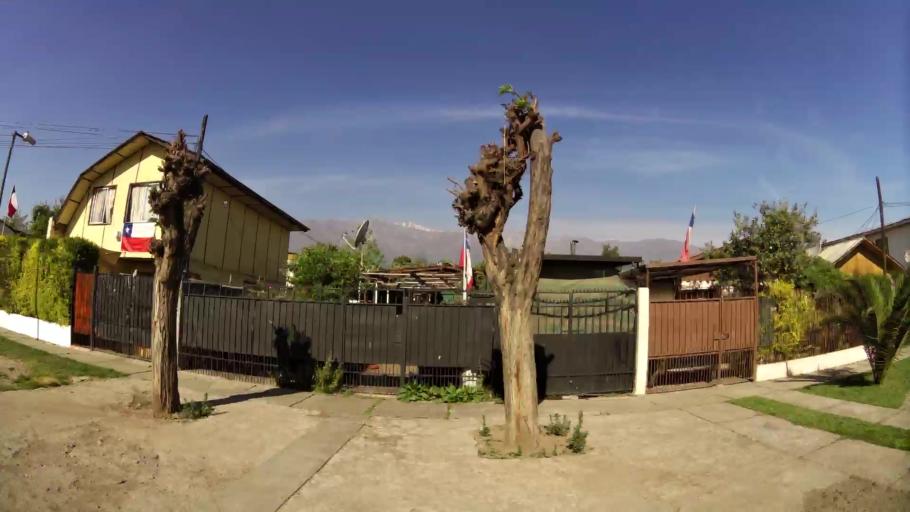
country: CL
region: Santiago Metropolitan
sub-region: Provincia de Santiago
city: Villa Presidente Frei, Nunoa, Santiago, Chile
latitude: -33.4657
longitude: -70.5611
